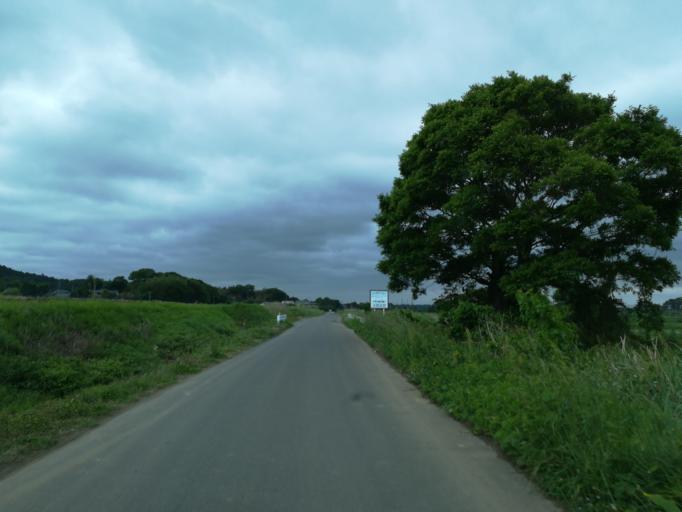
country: JP
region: Ibaraki
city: Tsukuba
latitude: 36.1958
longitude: 140.1064
